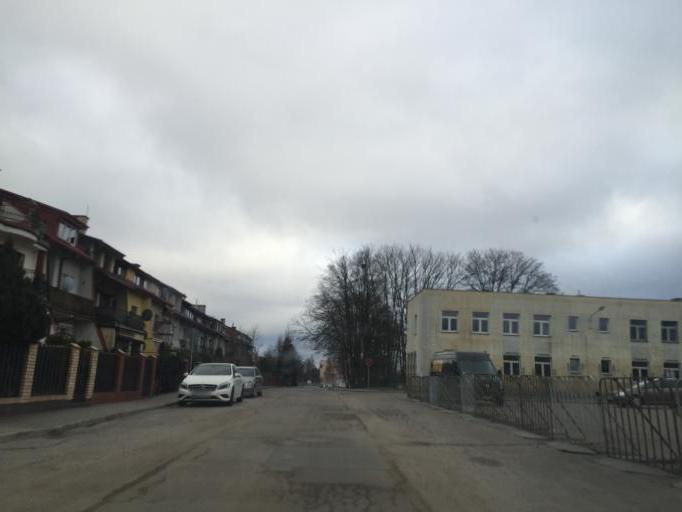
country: PL
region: Pomeranian Voivodeship
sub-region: Sopot
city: Sopot
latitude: 54.3783
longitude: 18.5227
